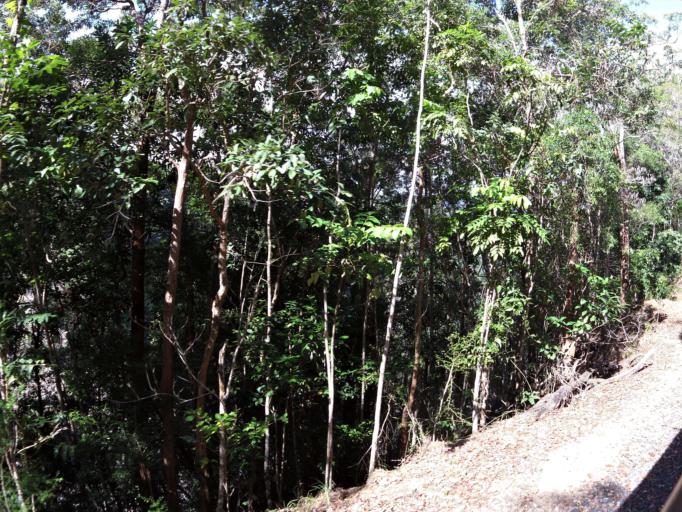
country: AU
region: Queensland
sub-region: Tablelands
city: Kuranda
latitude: -16.8338
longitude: 145.6423
